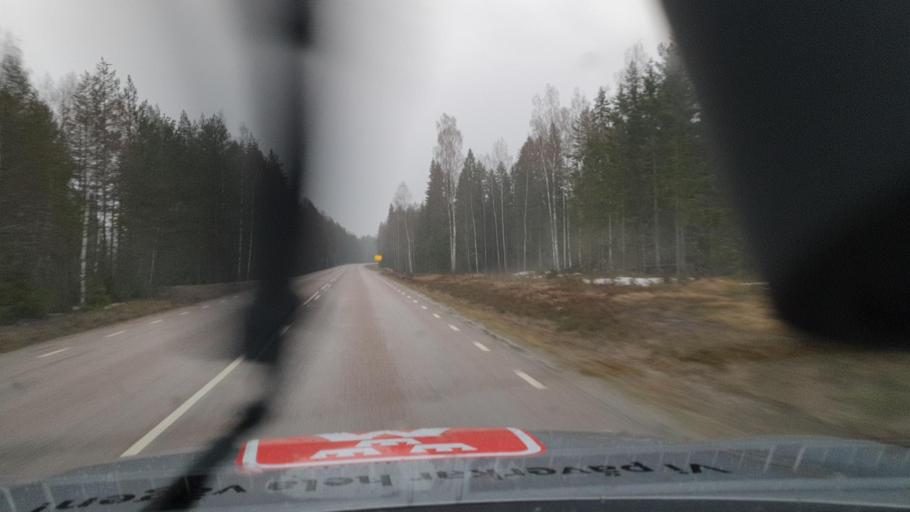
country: SE
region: Vaesternorrland
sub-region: OErnskoeldsviks Kommun
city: Bjasta
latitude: 63.2267
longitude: 18.4557
